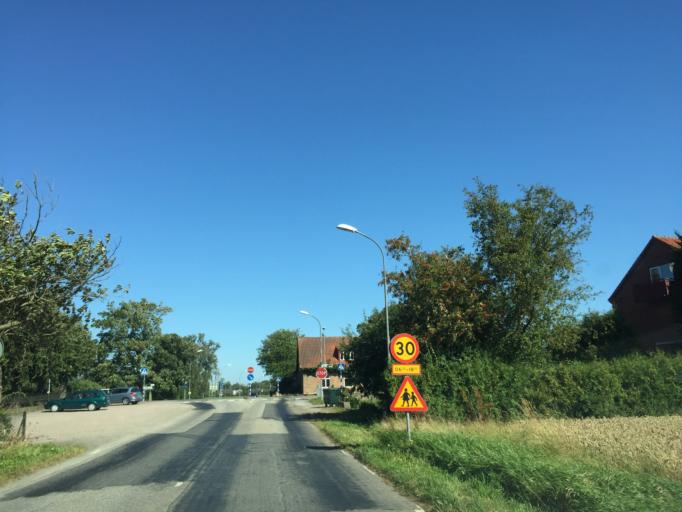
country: SE
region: Skane
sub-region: Ystads Kommun
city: Kopingebro
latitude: 55.4280
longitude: 14.1134
